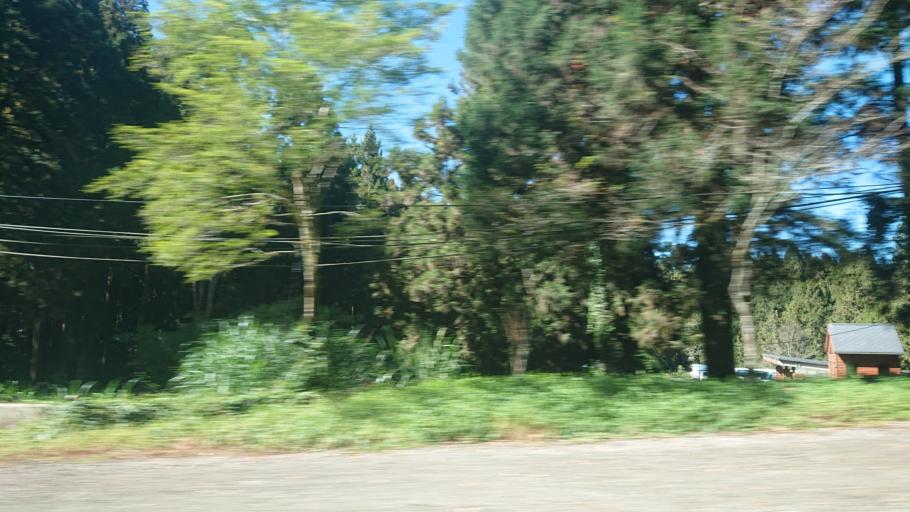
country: TW
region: Taiwan
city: Lugu
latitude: 23.5037
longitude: 120.7931
